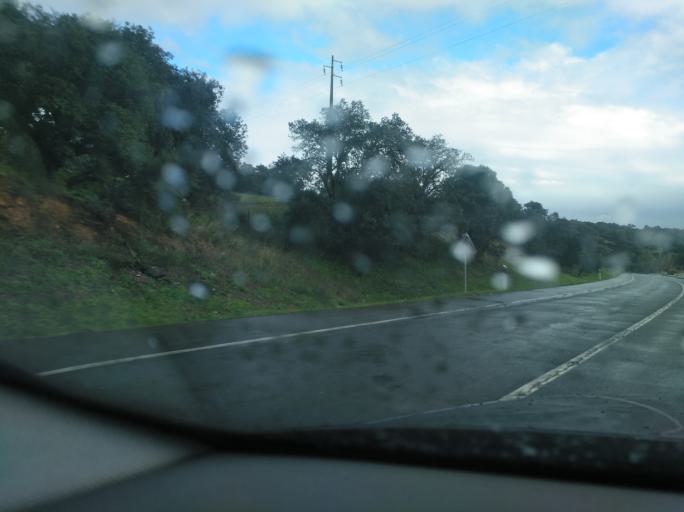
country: PT
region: Setubal
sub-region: Grandola
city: Grandola
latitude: 38.0664
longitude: -8.4125
